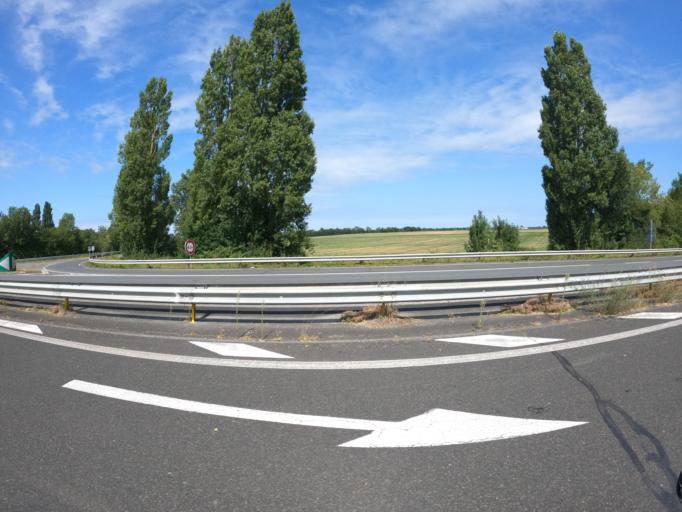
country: FR
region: Poitou-Charentes
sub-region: Departement des Deux-Sevres
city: Frontenay-Rohan-Rohan
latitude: 46.2608
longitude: -0.5368
